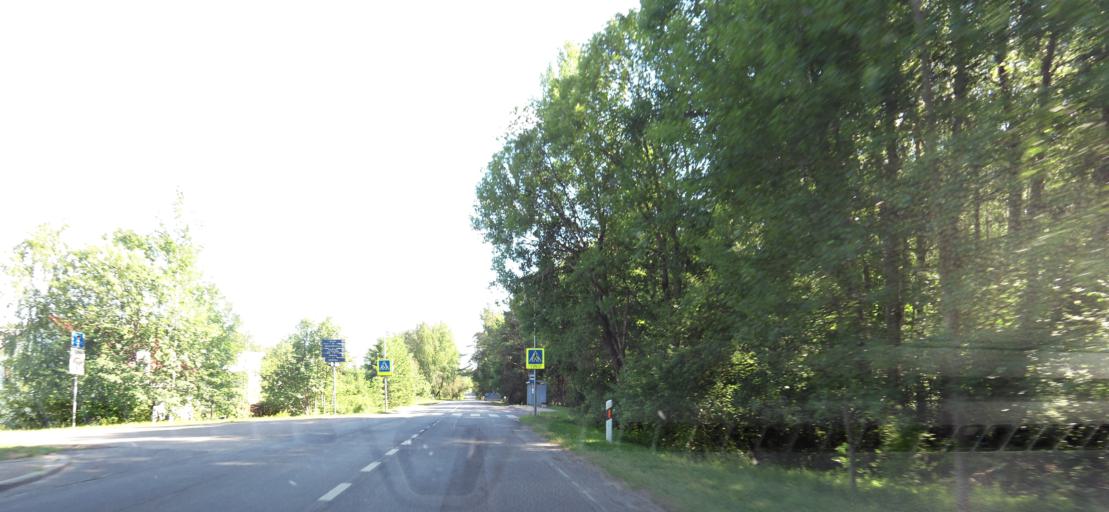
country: LT
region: Vilnius County
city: Rasos
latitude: 54.7957
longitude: 25.3499
